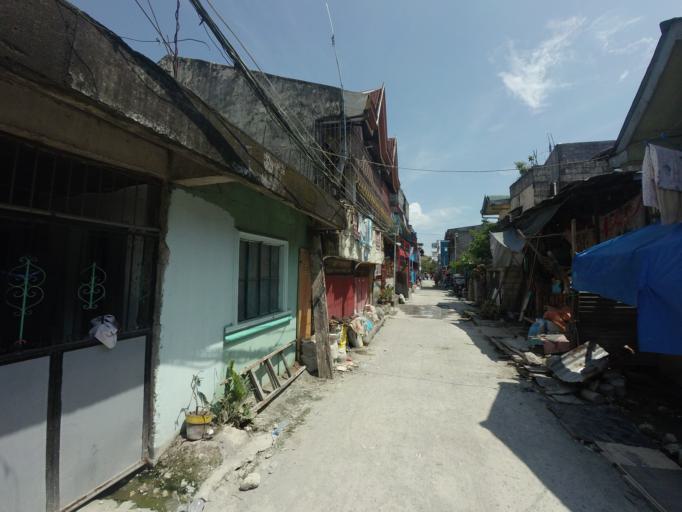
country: PH
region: Calabarzon
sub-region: Province of Rizal
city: Taytay
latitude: 14.5388
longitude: 121.1097
